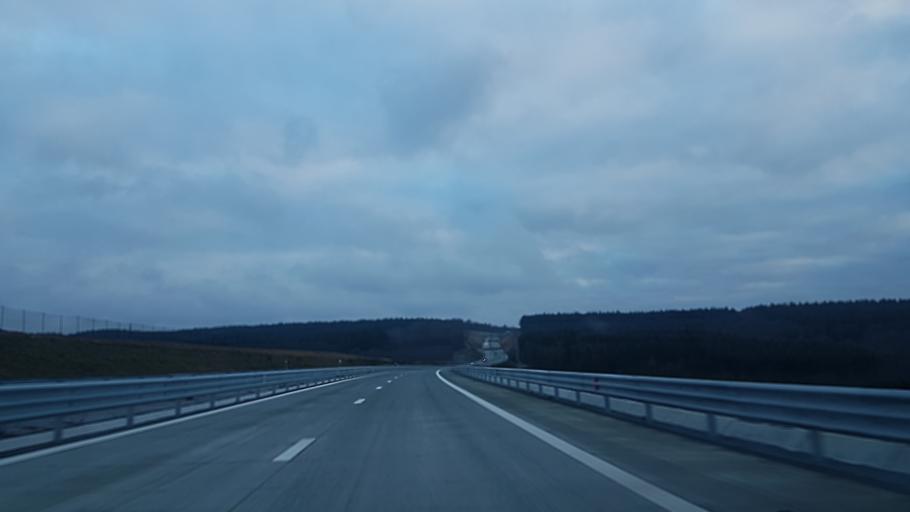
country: BE
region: Wallonia
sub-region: Province de Namur
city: Couvin
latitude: 50.0129
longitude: 4.5345
